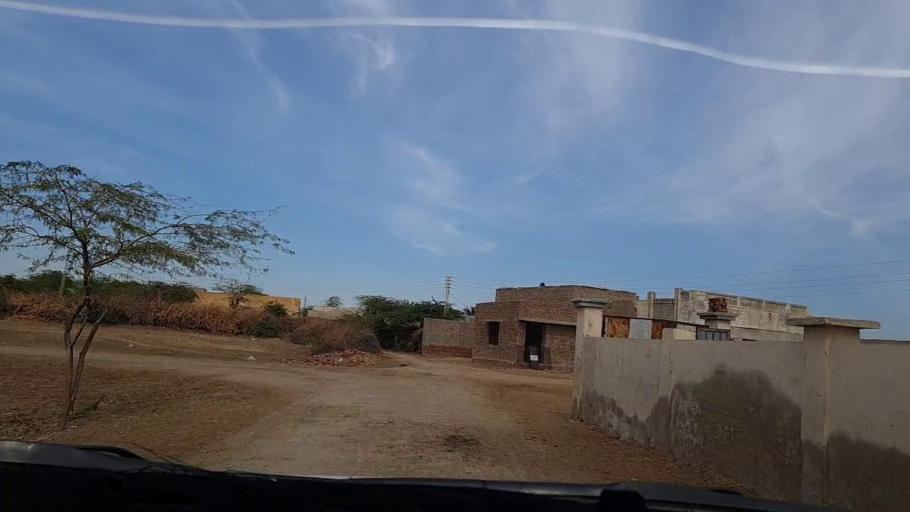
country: PK
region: Sindh
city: Dhoro Naro
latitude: 25.4765
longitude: 69.4798
